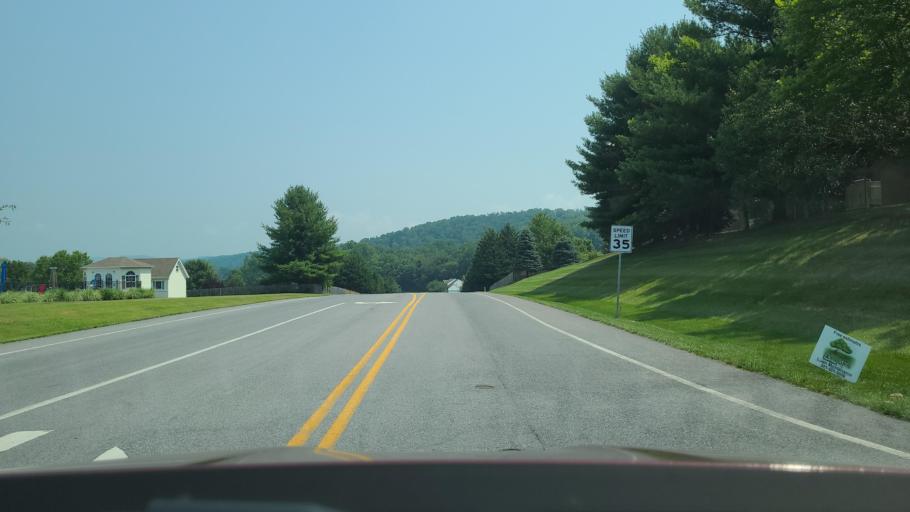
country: US
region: Maryland
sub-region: Frederick County
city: Jefferson
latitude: 39.3654
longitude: -77.5254
